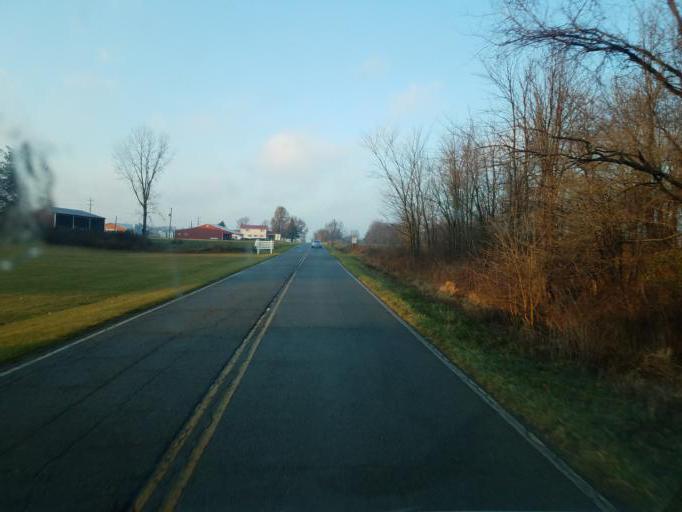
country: US
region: Ohio
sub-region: Knox County
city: Centerburg
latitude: 40.2467
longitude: -82.6909
